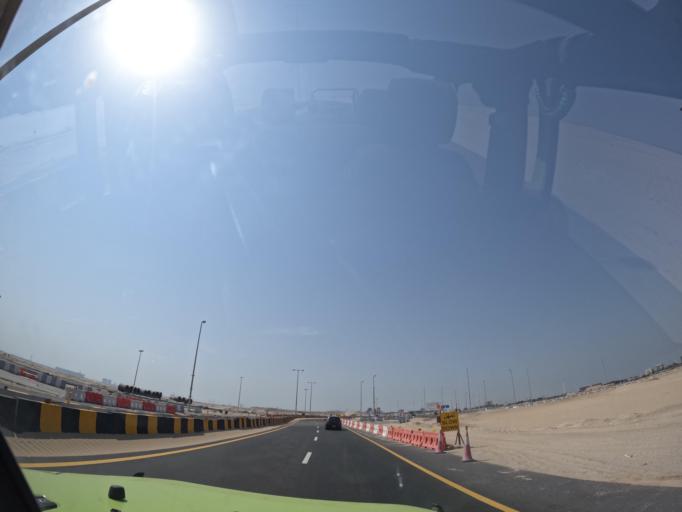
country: AE
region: Abu Dhabi
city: Abu Dhabi
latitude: 24.3864
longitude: 54.5808
